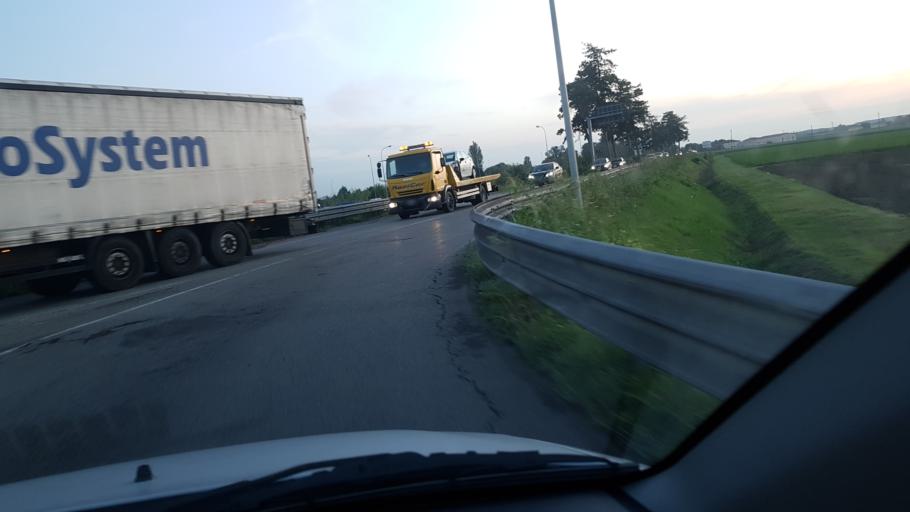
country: IT
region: Emilia-Romagna
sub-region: Provincia di Modena
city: Cavezzo
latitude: 44.8218
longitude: 11.0439
